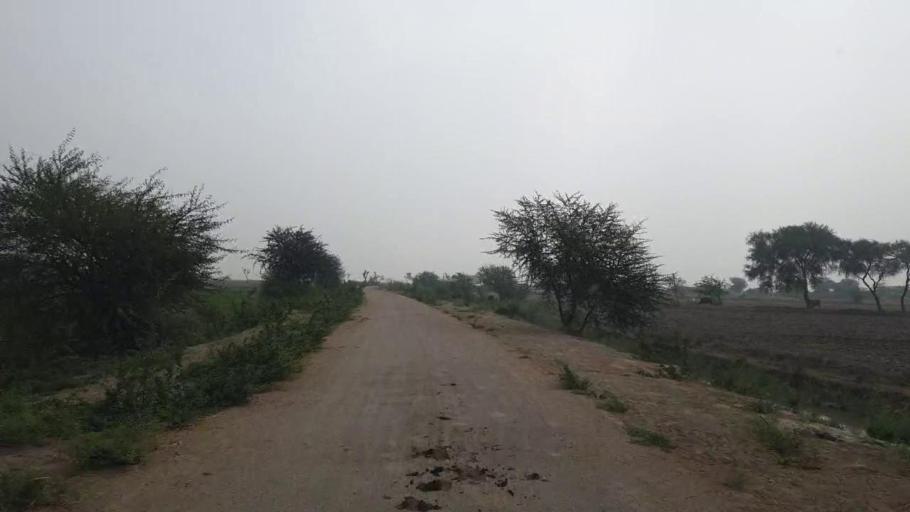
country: PK
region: Sindh
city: Badin
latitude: 24.5743
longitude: 68.6864
